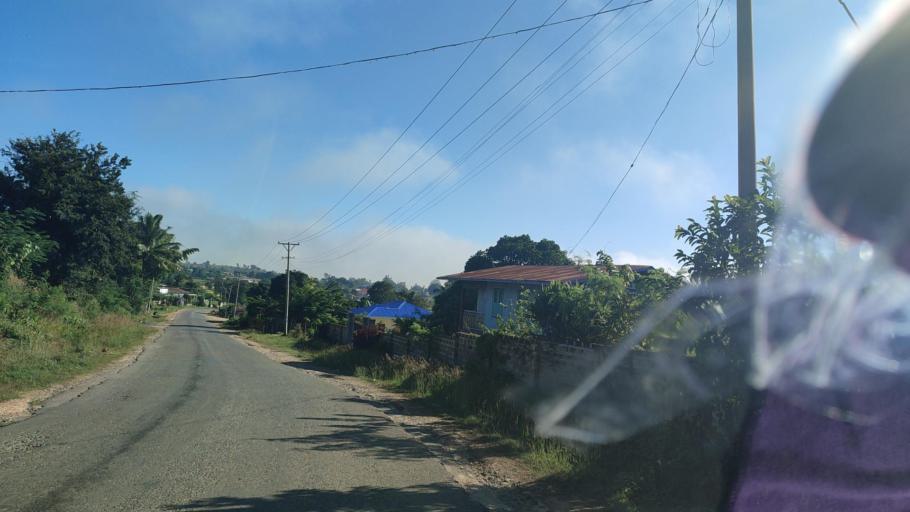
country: MM
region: Shan
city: Taunggyi
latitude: 20.9248
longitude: 97.6527
